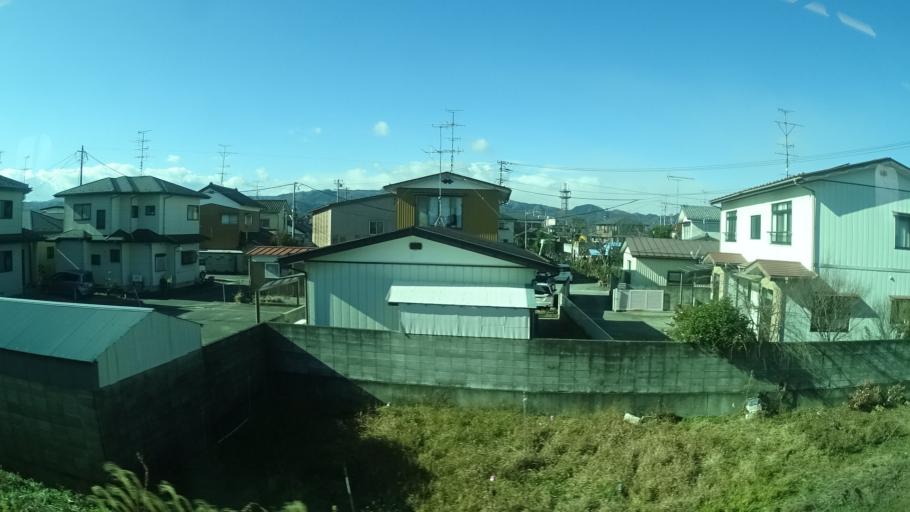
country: JP
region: Miyagi
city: Marumori
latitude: 37.7953
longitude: 140.9269
